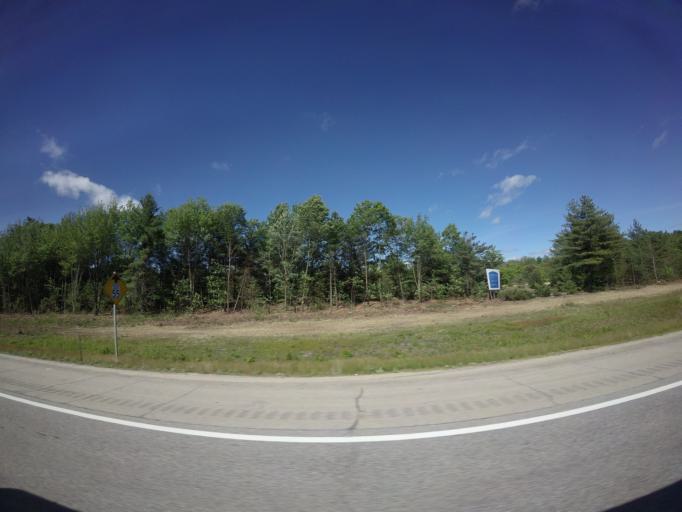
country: US
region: New Hampshire
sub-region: Rockingham County
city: Auburn
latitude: 42.9469
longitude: -71.3932
